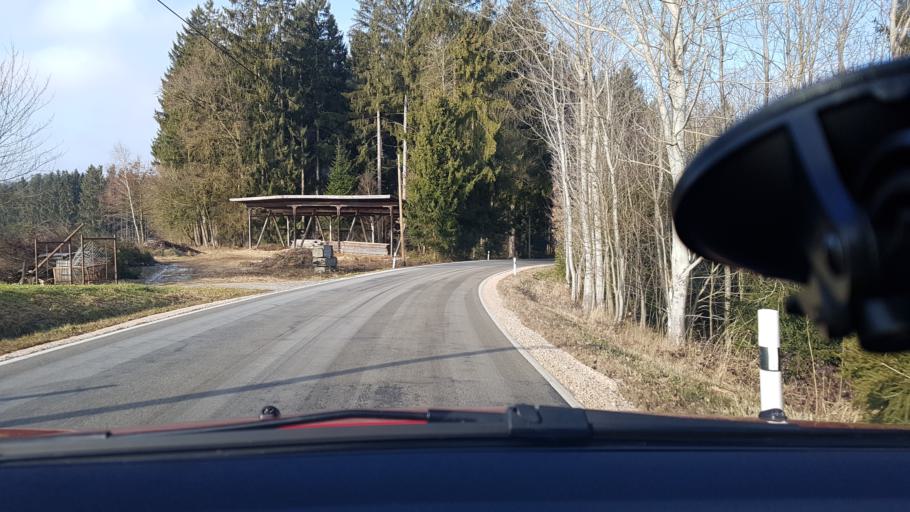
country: DE
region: Bavaria
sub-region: Lower Bavaria
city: Wittibreut
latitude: 48.3309
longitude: 12.9786
